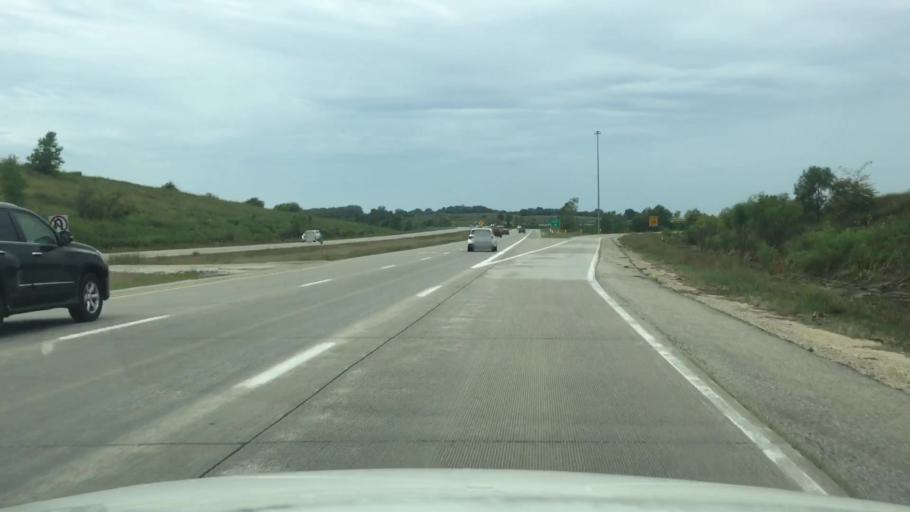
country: US
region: Iowa
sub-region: Polk County
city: West Des Moines
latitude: 41.5230
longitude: -93.7621
